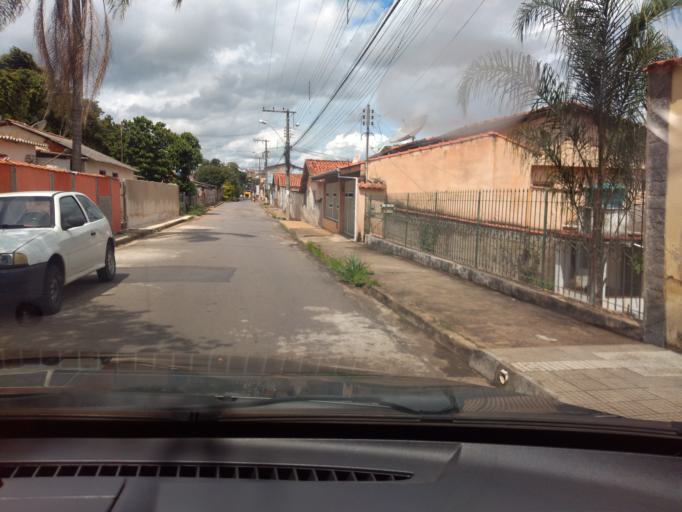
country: BR
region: Minas Gerais
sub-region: Tres Coracoes
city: Tres Coracoes
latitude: -21.6979
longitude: -45.2654
